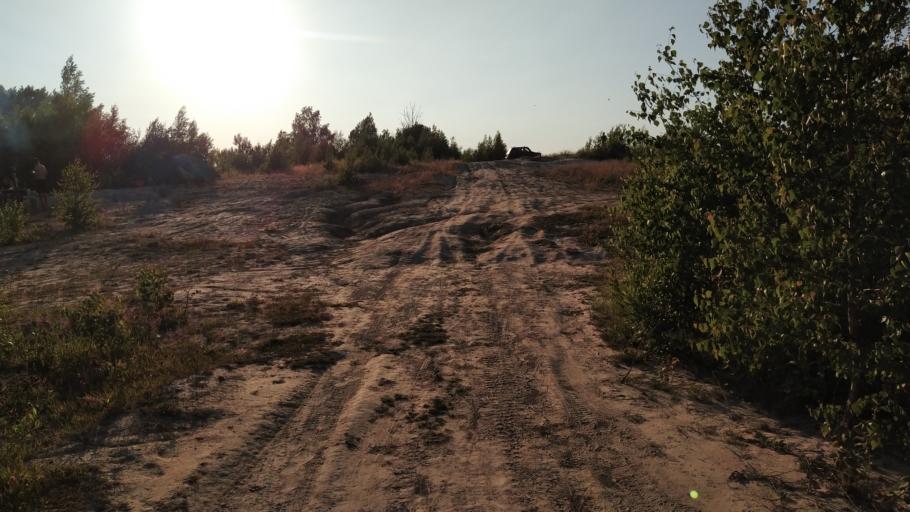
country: RU
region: Leningrad
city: Toksovo
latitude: 60.1127
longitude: 30.5410
